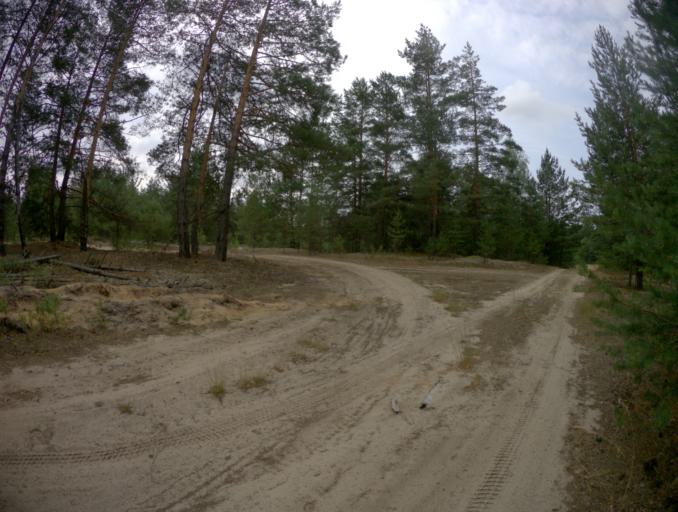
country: RU
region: Nizjnij Novgorod
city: Frolishchi
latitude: 56.3566
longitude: 42.6403
